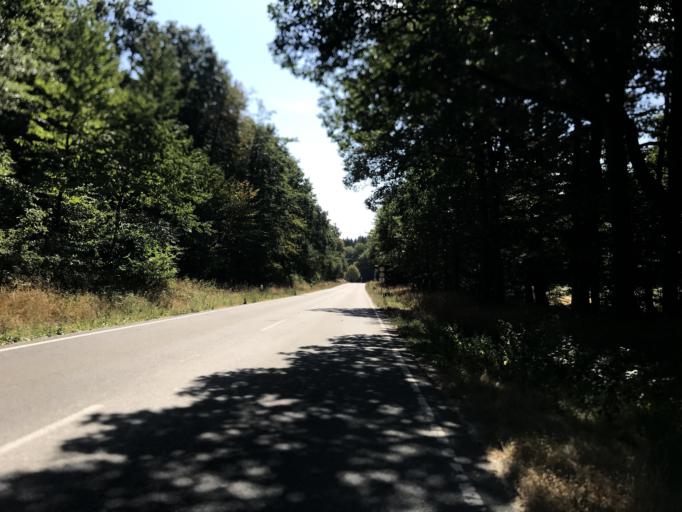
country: DE
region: Hesse
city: Geisenheim
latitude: 50.0243
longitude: 7.9570
